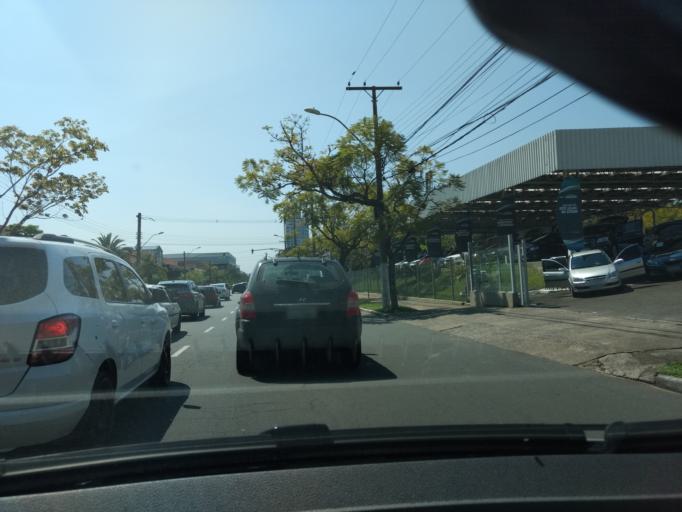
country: BR
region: Rio Grande do Sul
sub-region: Porto Alegre
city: Porto Alegre
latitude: -30.0276
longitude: -51.1612
